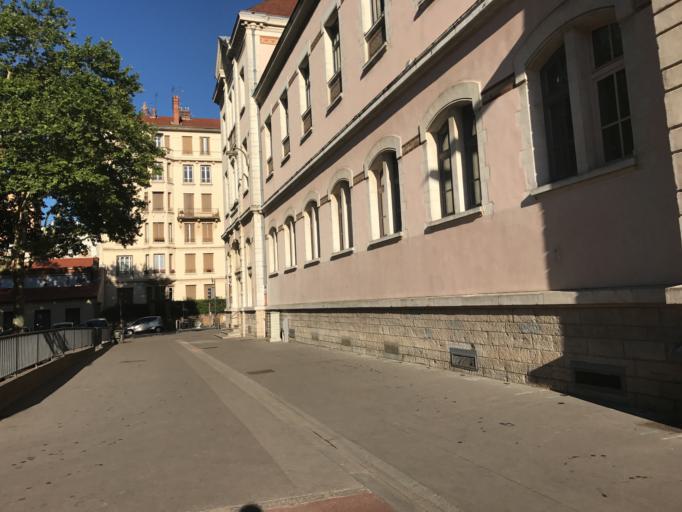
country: FR
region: Rhone-Alpes
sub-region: Departement du Rhone
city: Caluire-et-Cuire
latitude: 45.7796
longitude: 4.8354
